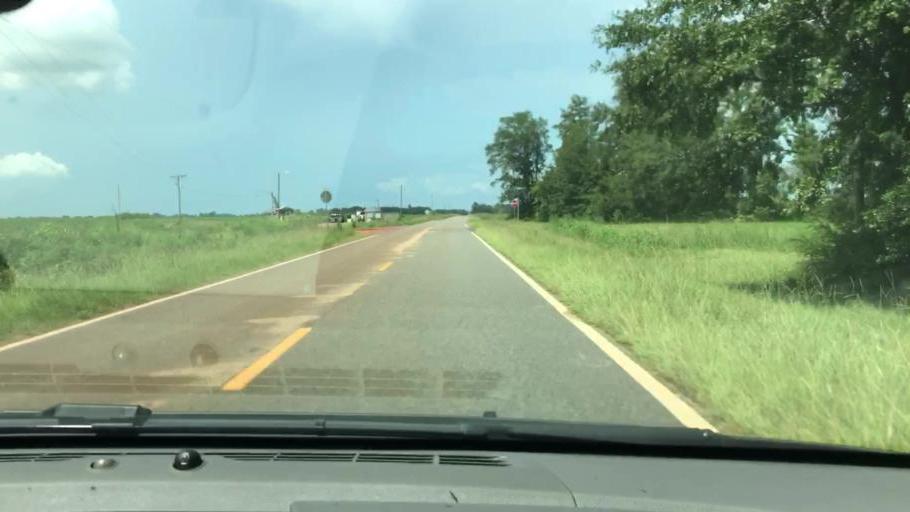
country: US
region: Georgia
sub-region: Seminole County
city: Donalsonville
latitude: 31.0973
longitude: -84.9962
